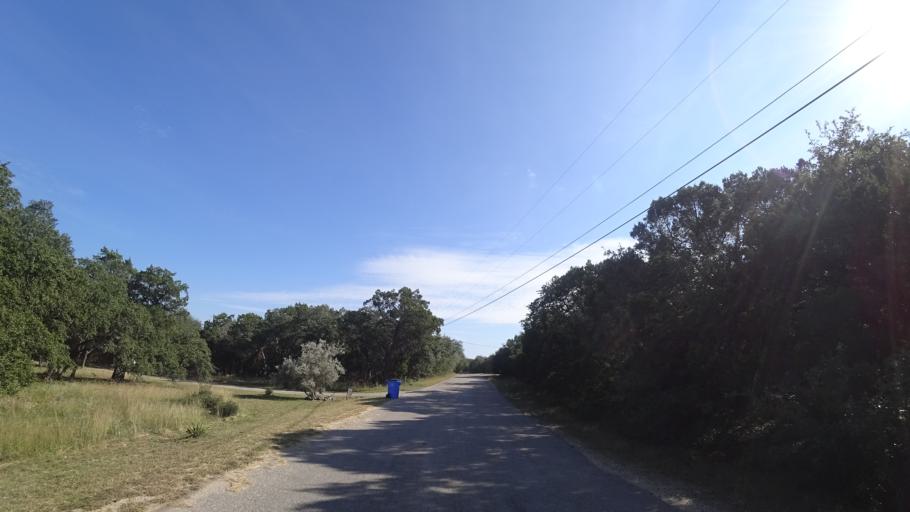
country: US
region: Texas
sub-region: Travis County
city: Bee Cave
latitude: 30.2322
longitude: -97.9384
